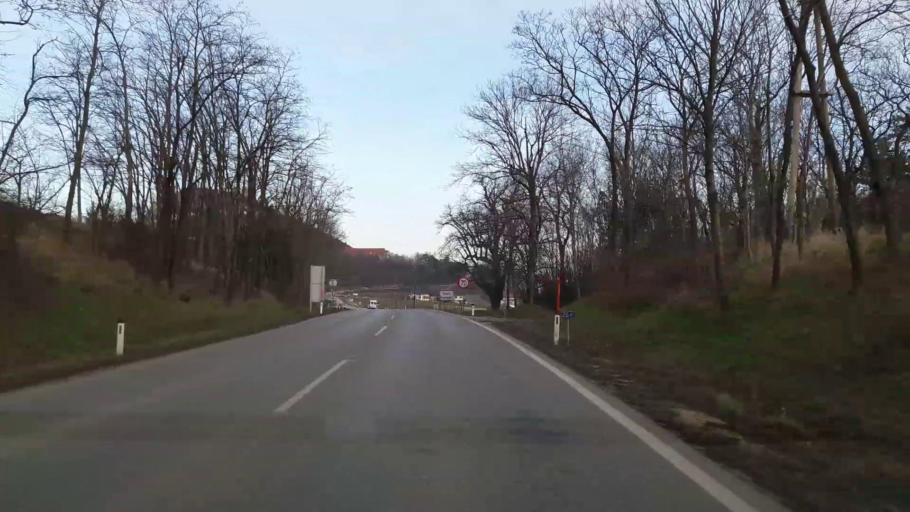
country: AT
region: Lower Austria
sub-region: Politischer Bezirk Mistelbach
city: Staatz
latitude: 48.6701
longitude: 16.4914
